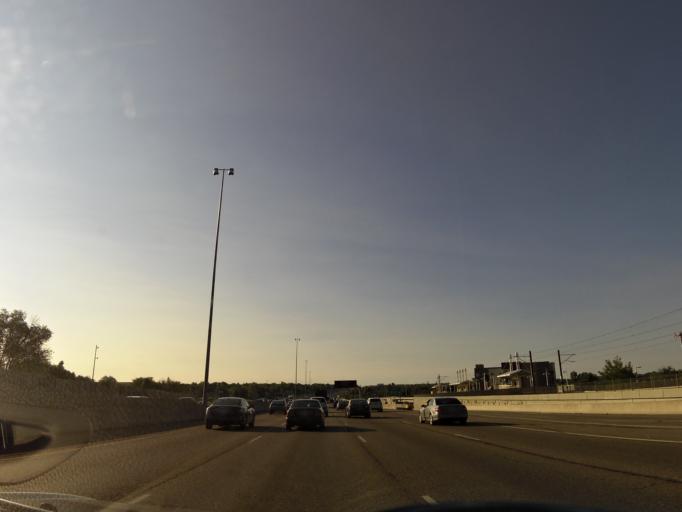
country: US
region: Colorado
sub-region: Arapahoe County
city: Glendale
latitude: 39.6701
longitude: -104.9276
